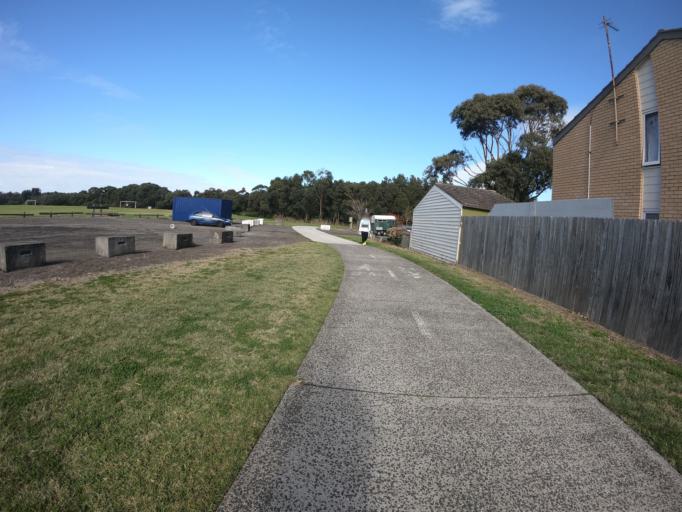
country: AU
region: New South Wales
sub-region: Wollongong
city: East Corrimal
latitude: -34.3697
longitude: 150.9237
